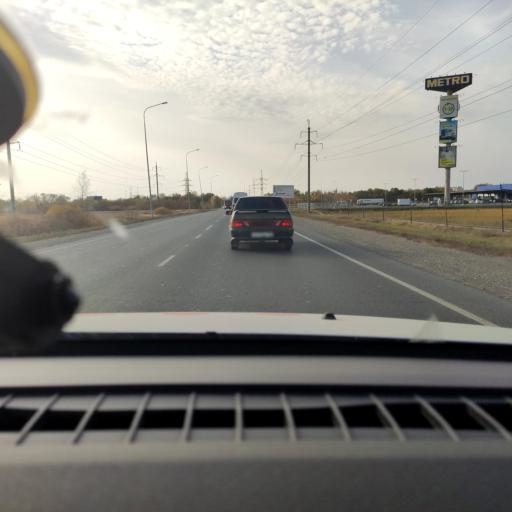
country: RU
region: Samara
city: Samara
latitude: 53.1315
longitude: 50.1418
